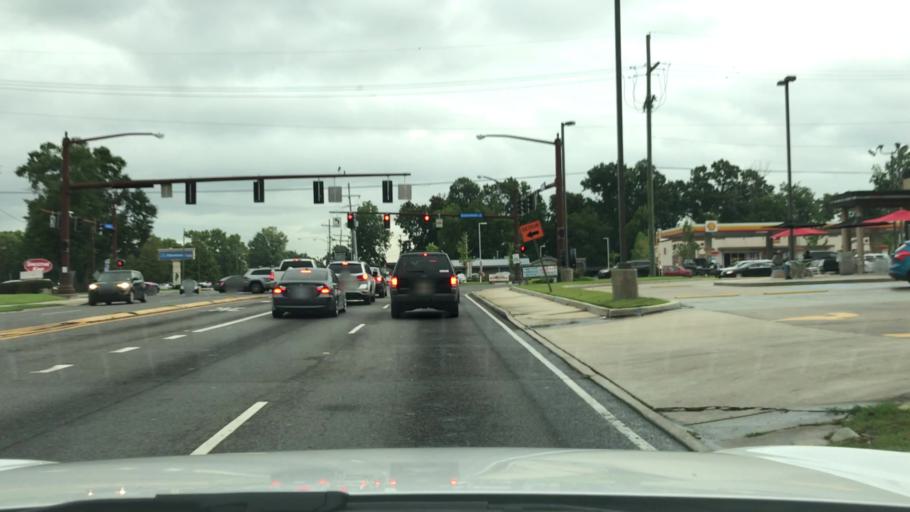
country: US
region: Louisiana
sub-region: East Baton Rouge Parish
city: Baton Rouge
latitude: 30.4439
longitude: -91.1384
